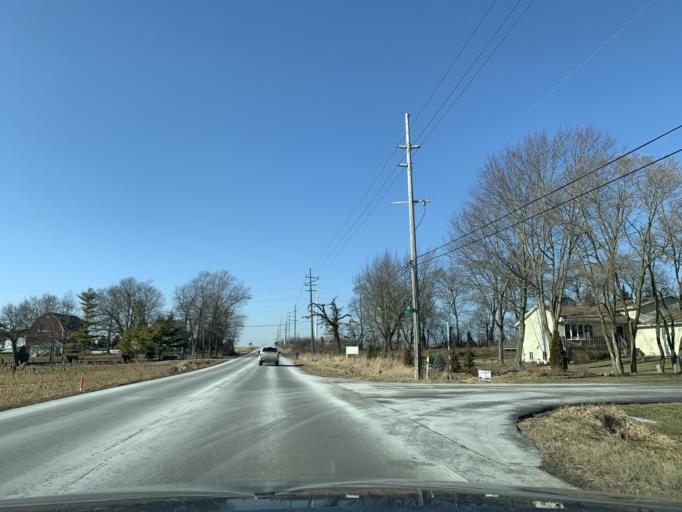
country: US
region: Indiana
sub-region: Lake County
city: Crown Point
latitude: 41.4209
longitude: -87.4202
